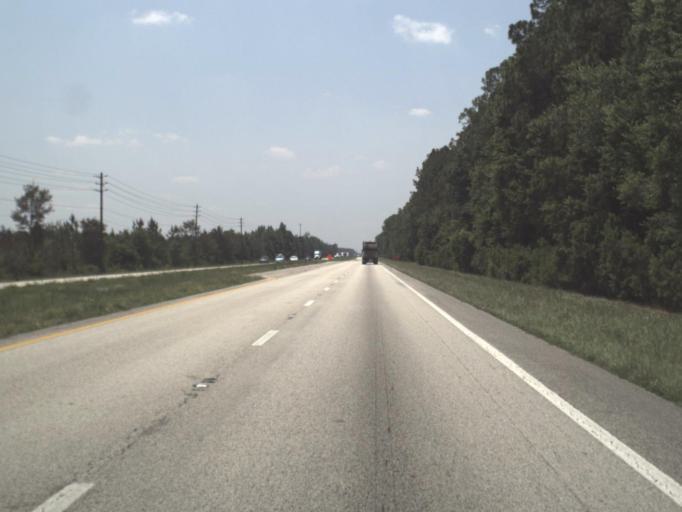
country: US
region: Florida
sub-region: Duval County
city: Baldwin
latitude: 30.2573
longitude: -81.9934
